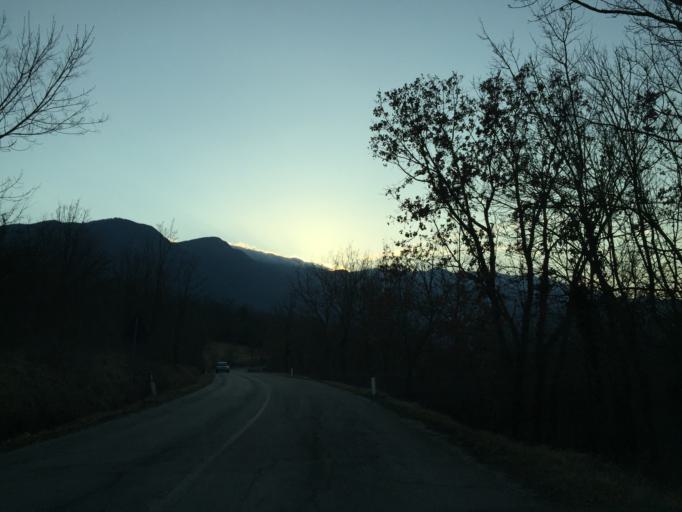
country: IT
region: Molise
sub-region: Provincia di Campobasso
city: Guardiaregia
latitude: 41.4492
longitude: 14.5547
